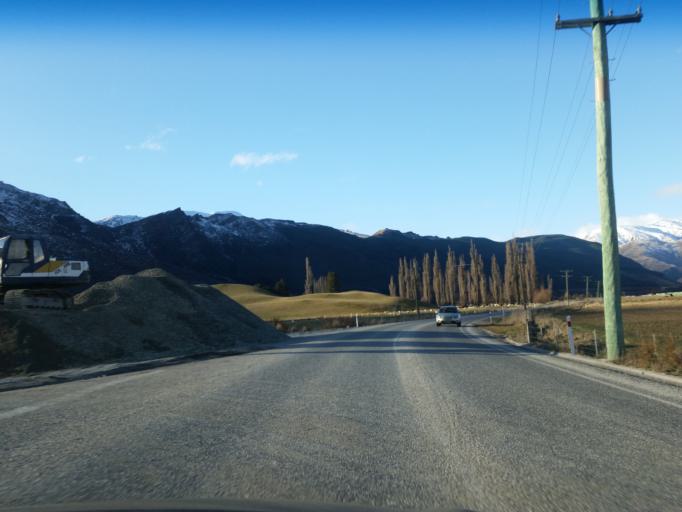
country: NZ
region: Otago
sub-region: Queenstown-Lakes District
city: Arrowtown
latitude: -44.9534
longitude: 168.7451
